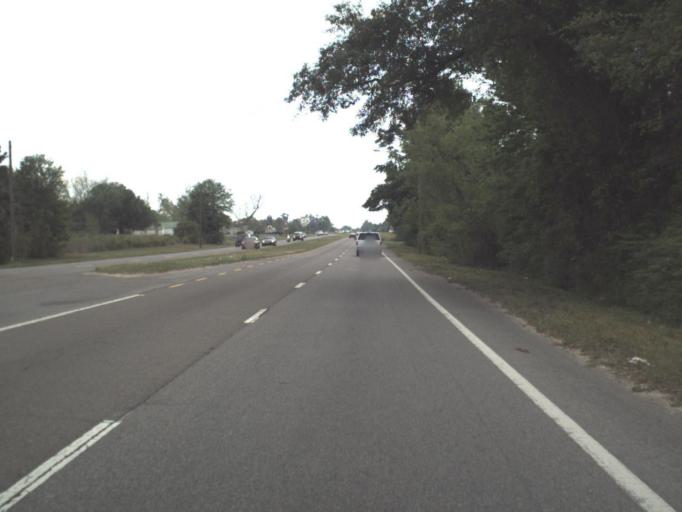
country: US
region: Florida
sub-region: Escambia County
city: Cantonment
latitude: 30.6045
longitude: -87.3161
